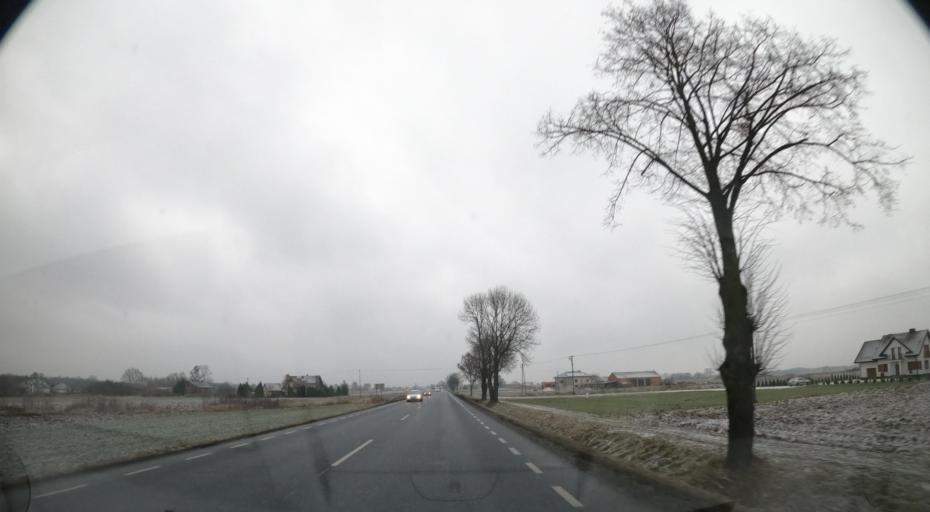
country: PL
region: Masovian Voivodeship
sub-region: Powiat sochaczewski
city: Mlodzieszyn
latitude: 52.2777
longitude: 20.1731
